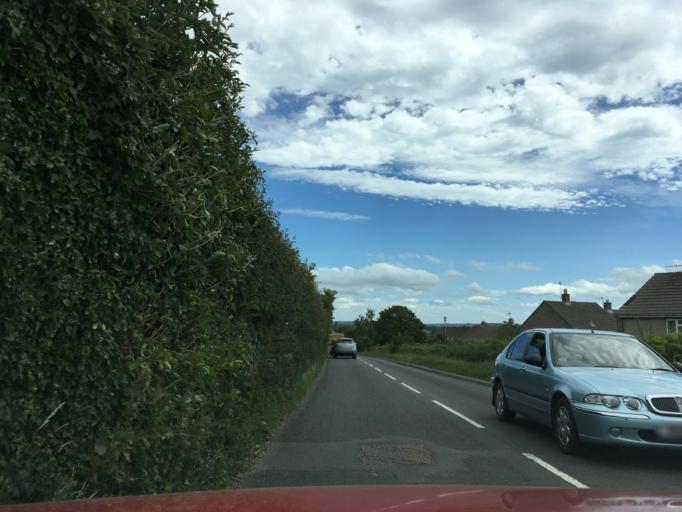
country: GB
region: England
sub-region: Somerset
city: Bradley Cross
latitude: 51.2382
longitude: -2.7229
